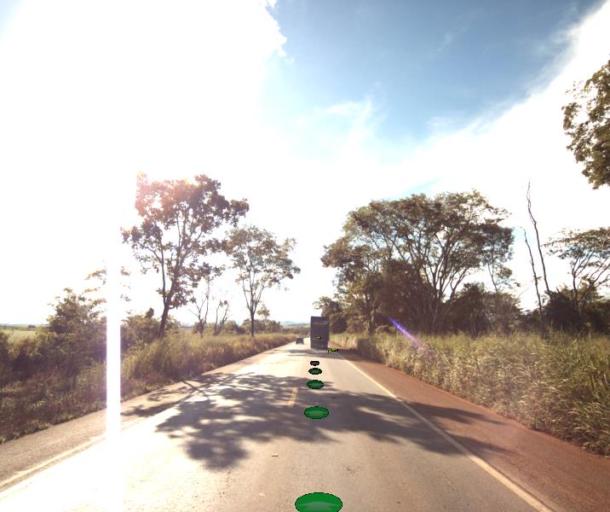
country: BR
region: Goias
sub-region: Rialma
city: Rialma
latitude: -15.4059
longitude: -49.5316
